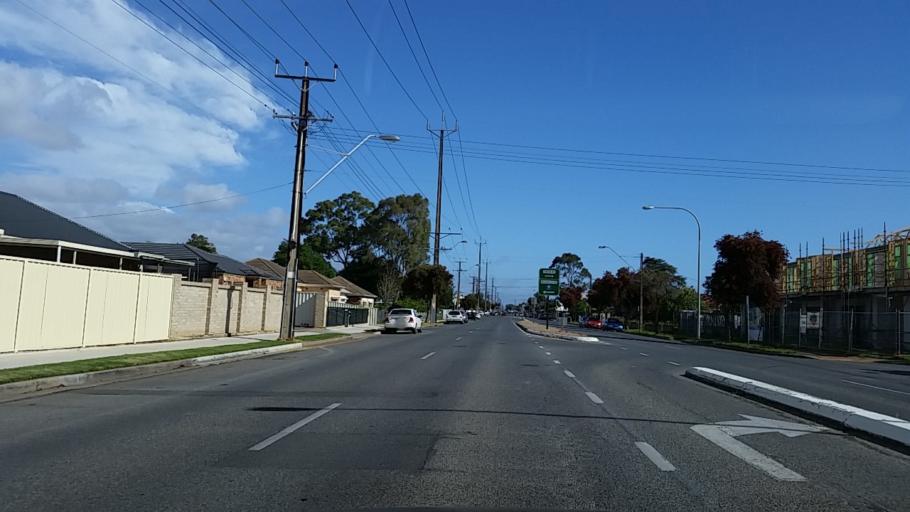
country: AU
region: South Australia
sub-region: Charles Sturt
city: Woodville West
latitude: -34.8831
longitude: 138.5310
